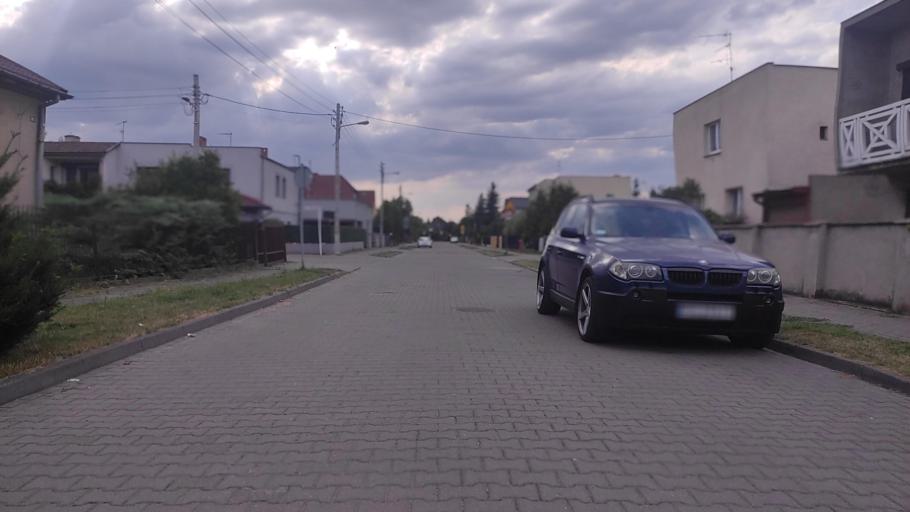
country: PL
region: Greater Poland Voivodeship
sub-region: Powiat poznanski
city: Swarzedz
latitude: 52.4040
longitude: 17.0823
